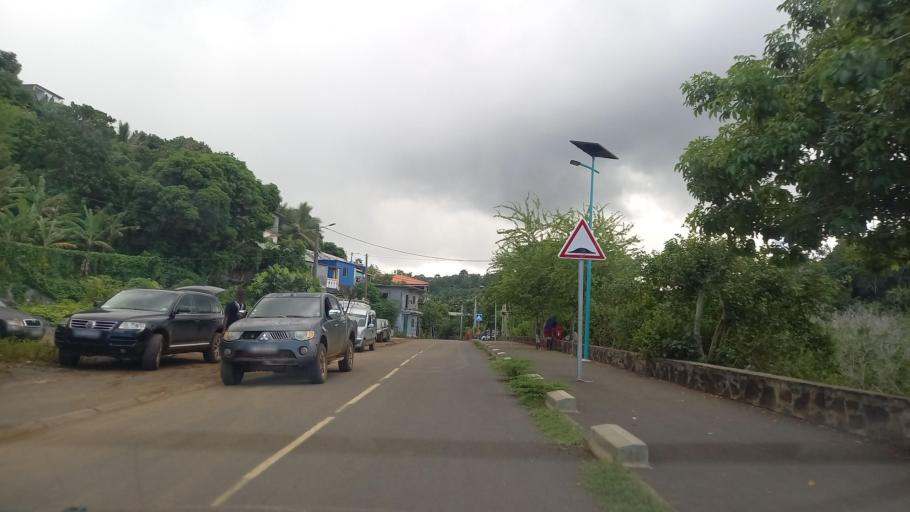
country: YT
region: Chiconi
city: Chiconi
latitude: -12.8389
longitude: 45.1158
